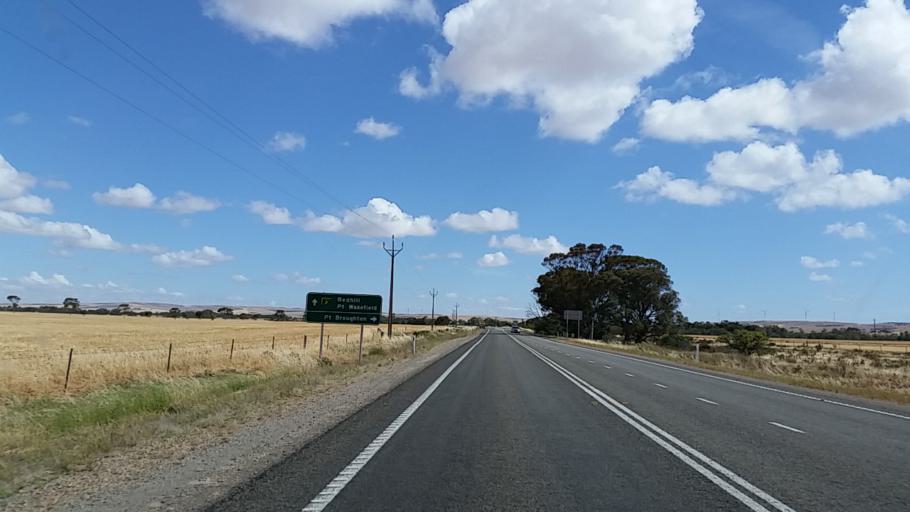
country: AU
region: South Australia
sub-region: Port Pirie City and Dists
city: Crystal Brook
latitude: -33.4276
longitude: 138.1554
